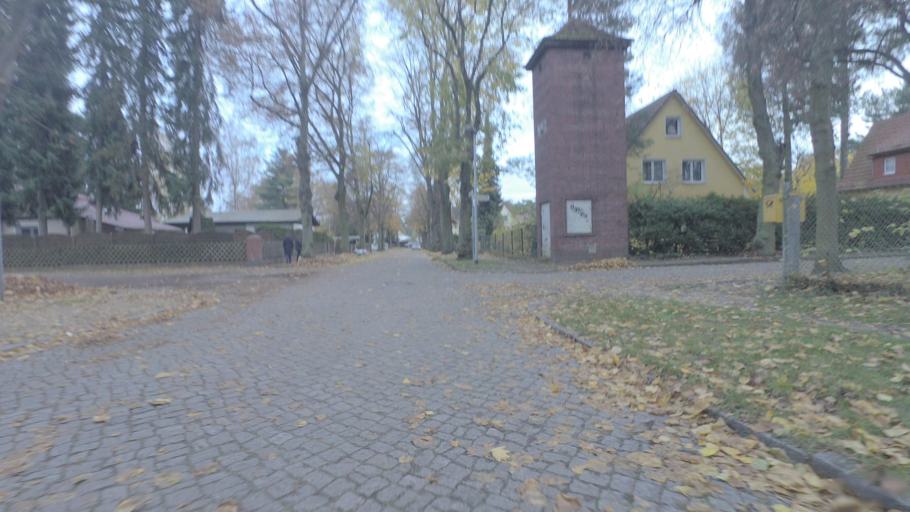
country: DE
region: Brandenburg
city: Rangsdorf
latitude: 52.2995
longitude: 13.4246
